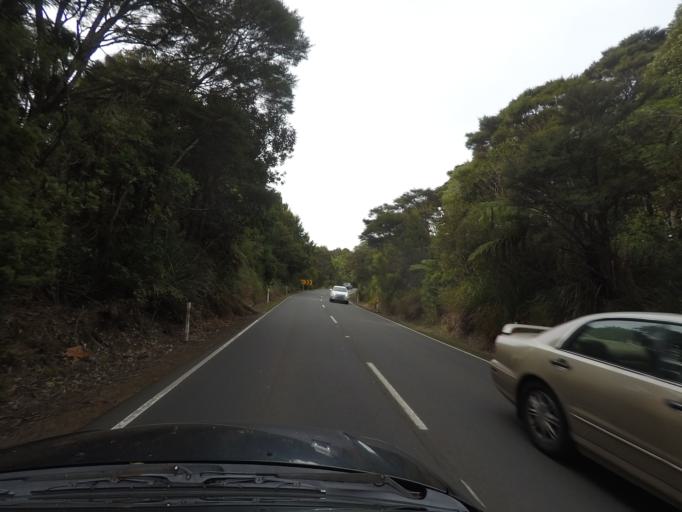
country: NZ
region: Auckland
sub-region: Auckland
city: Titirangi
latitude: -36.9328
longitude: 174.5690
